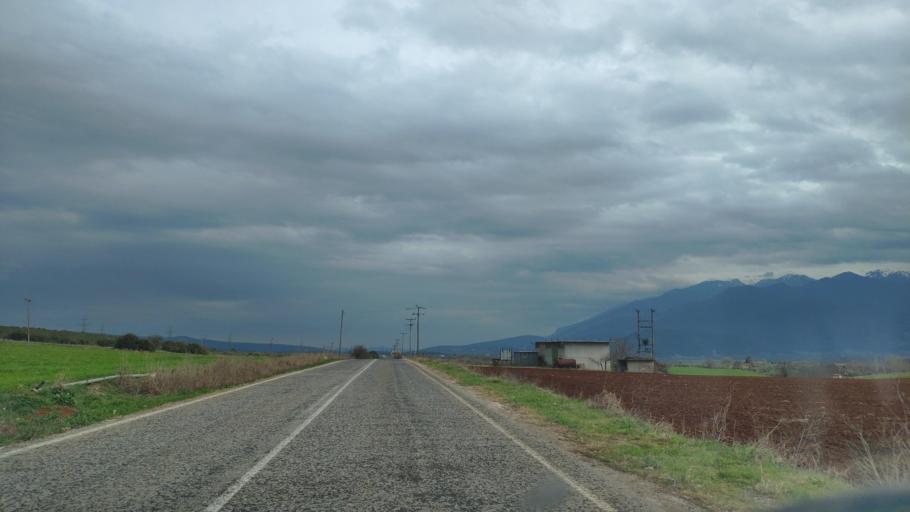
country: GR
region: Central Greece
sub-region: Nomos Fthiotidos
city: Amfikleia
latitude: 38.7046
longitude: 22.5057
